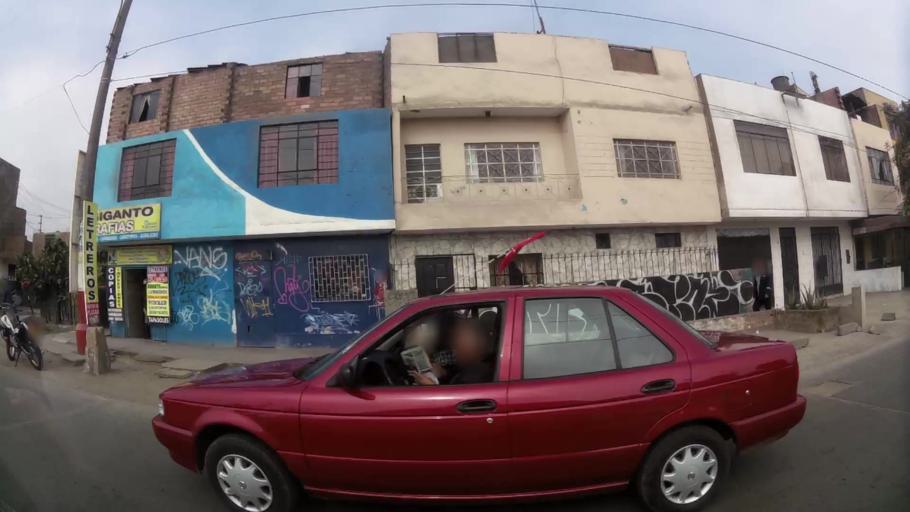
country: PE
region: Callao
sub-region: Callao
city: Callao
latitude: -12.0305
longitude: -77.0946
